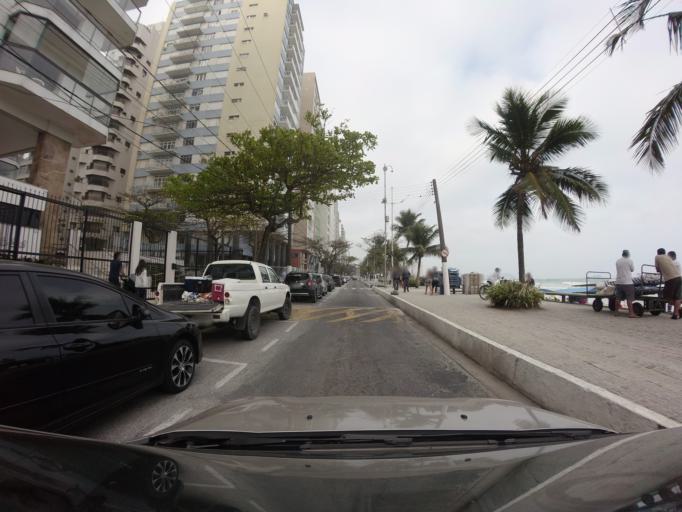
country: BR
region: Sao Paulo
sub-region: Guaruja
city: Guaruja
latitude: -23.9994
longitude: -46.2610
